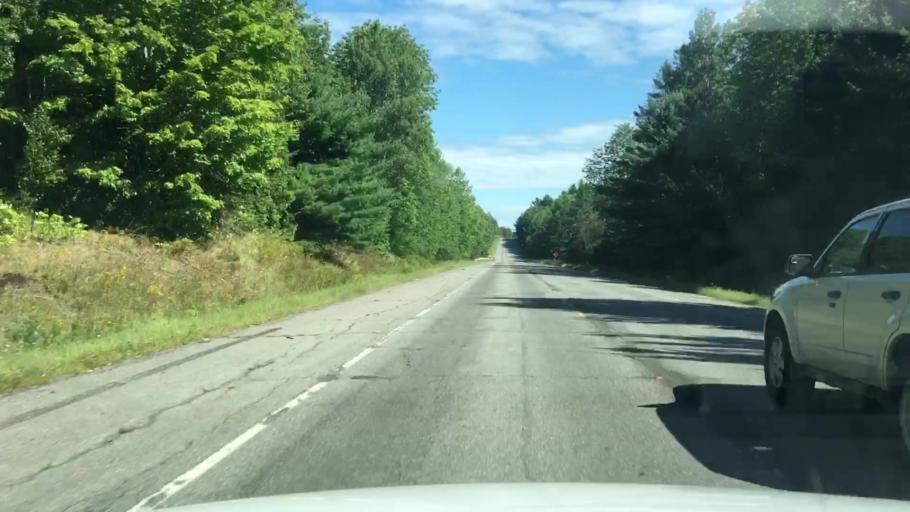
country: US
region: Maine
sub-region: Penobscot County
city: Dexter
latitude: 45.0541
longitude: -69.2579
